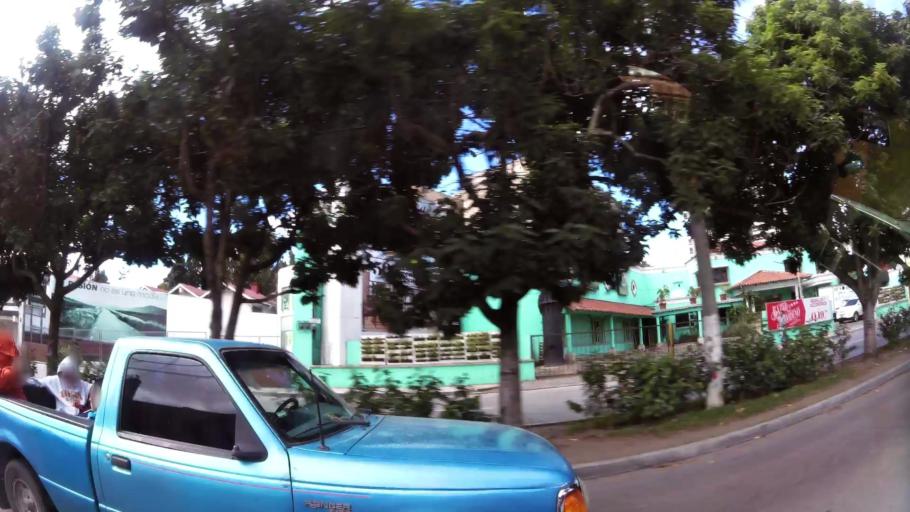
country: GT
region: Guatemala
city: Santa Catarina Pinula
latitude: 14.5972
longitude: -90.5074
